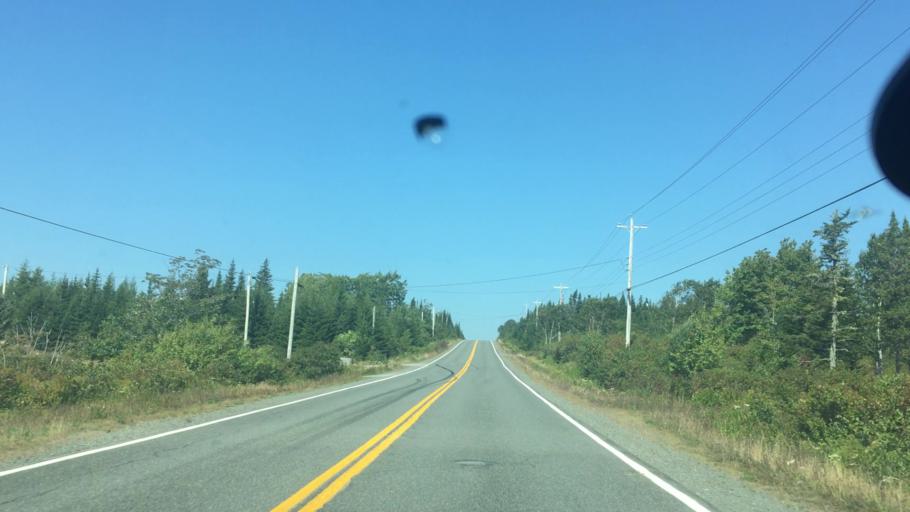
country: CA
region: Nova Scotia
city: Antigonish
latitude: 45.0020
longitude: -62.1008
